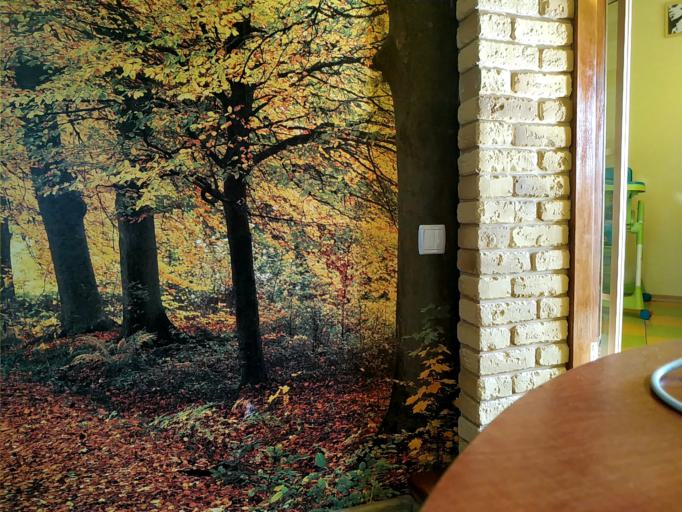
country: RU
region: Tverskaya
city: Kalashnikovo
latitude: 57.3433
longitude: 35.2536
